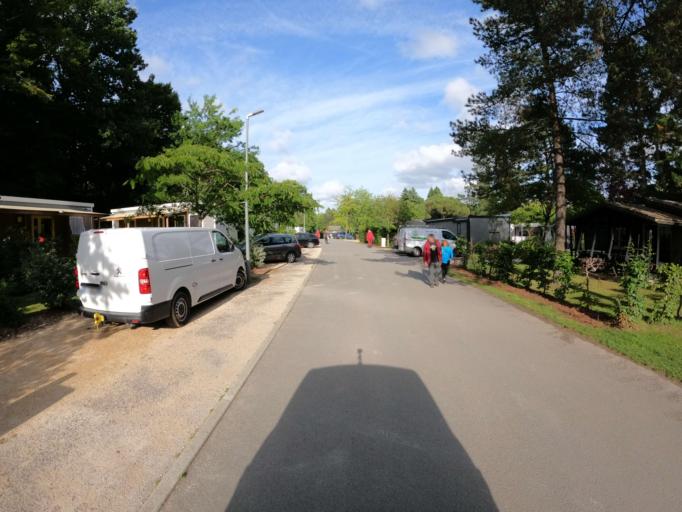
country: FR
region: Pays de la Loire
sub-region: Departement de la Loire-Atlantique
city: Nantes
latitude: 47.2429
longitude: -1.5597
